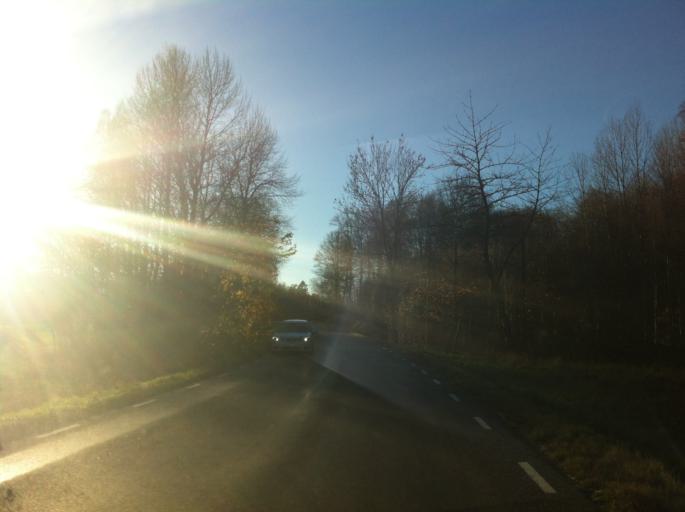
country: SE
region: Blekinge
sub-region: Olofstroms Kommun
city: Jamshog
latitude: 56.1856
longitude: 14.5861
